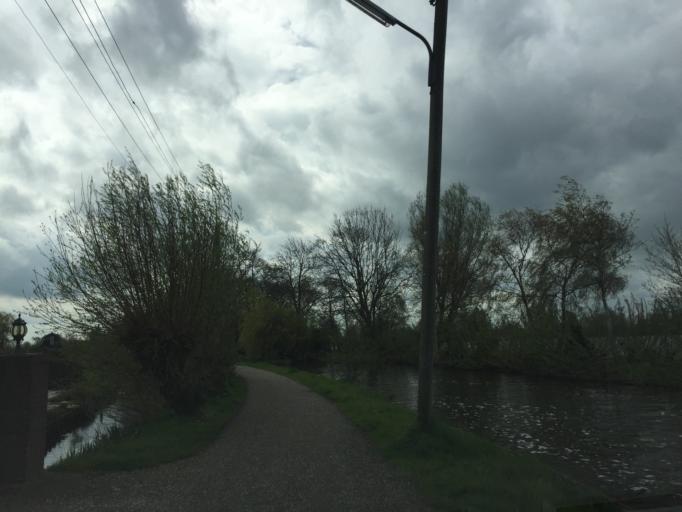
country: NL
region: South Holland
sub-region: Bodegraven-Reeuwijk
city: Reeuwijk
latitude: 52.0343
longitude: 4.7546
